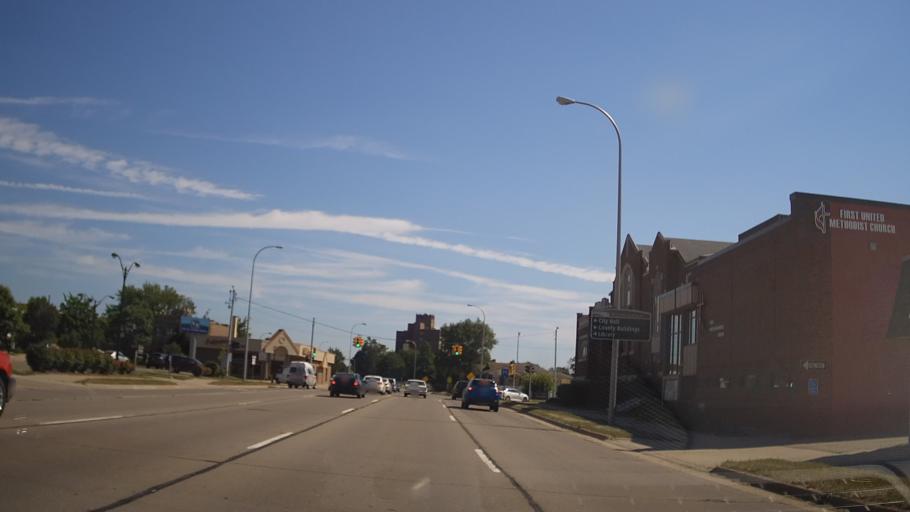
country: US
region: Michigan
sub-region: Macomb County
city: Mount Clemens
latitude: 42.5980
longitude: -82.8808
